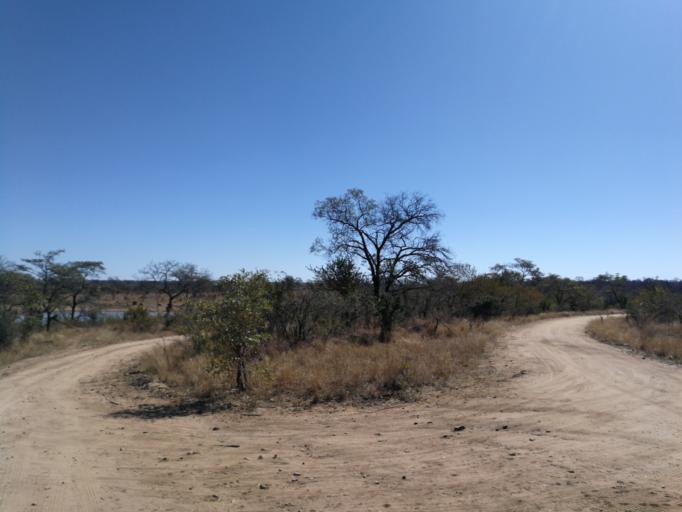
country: ZA
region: Limpopo
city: Thulamahashi
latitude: -24.8583
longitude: 31.7543
